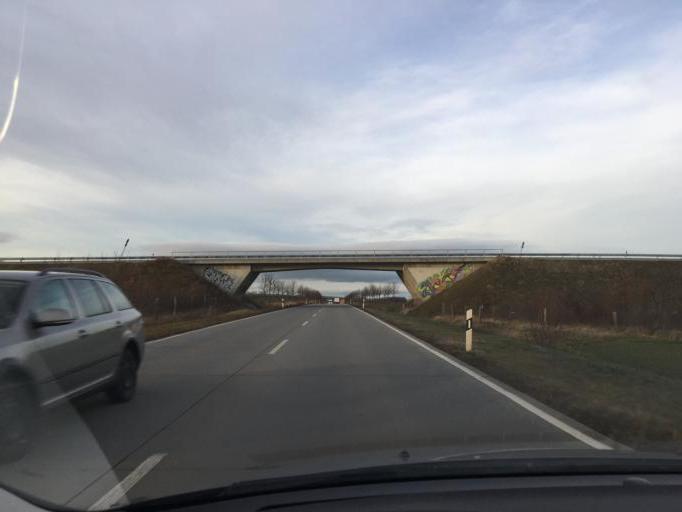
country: DE
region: Saxony
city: Grossposna
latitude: 51.2729
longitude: 12.4532
